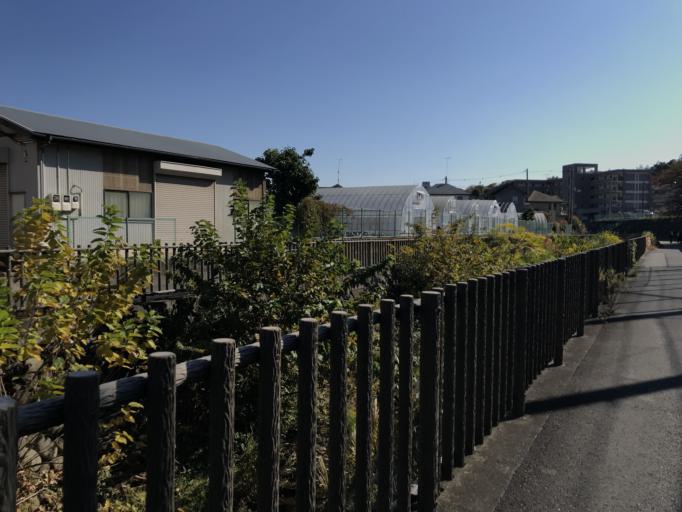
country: JP
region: Tokyo
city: Chofugaoka
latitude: 35.6019
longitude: 139.5499
